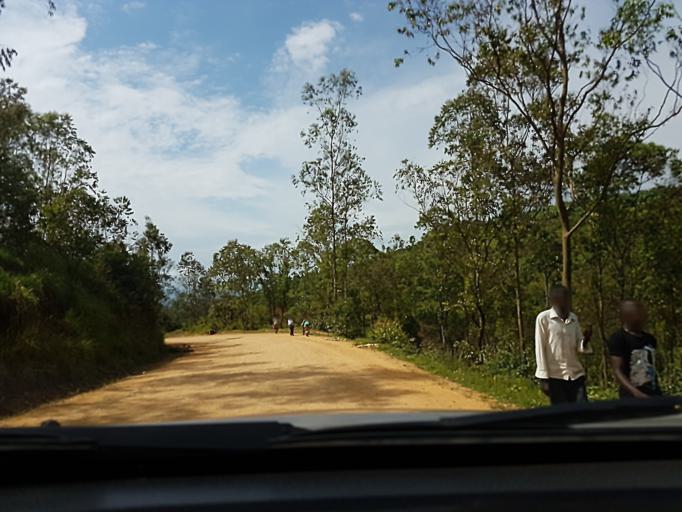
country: CD
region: South Kivu
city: Bukavu
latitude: -2.6332
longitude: 28.8755
